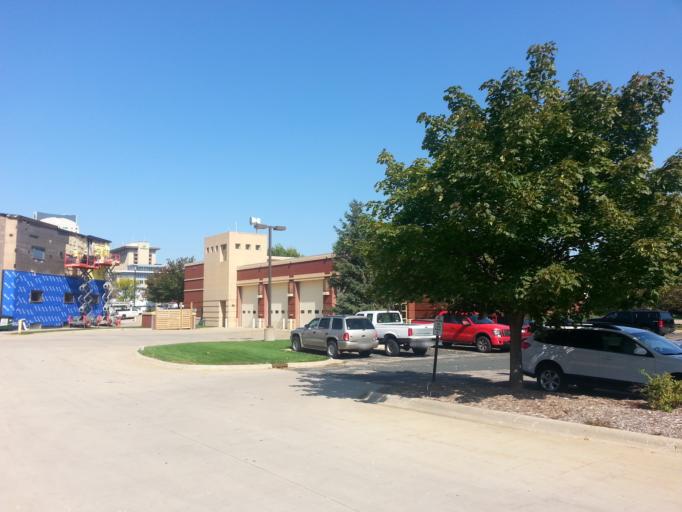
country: US
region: Minnesota
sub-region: Olmsted County
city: Rochester
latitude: 44.0172
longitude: -92.4641
